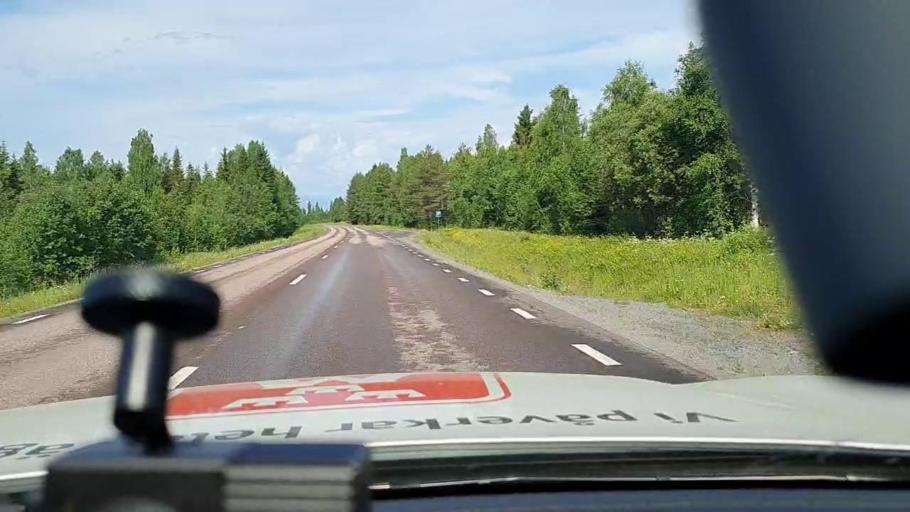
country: SE
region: Norrbotten
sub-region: Alvsbyns Kommun
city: AElvsbyn
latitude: 66.0213
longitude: 21.1338
